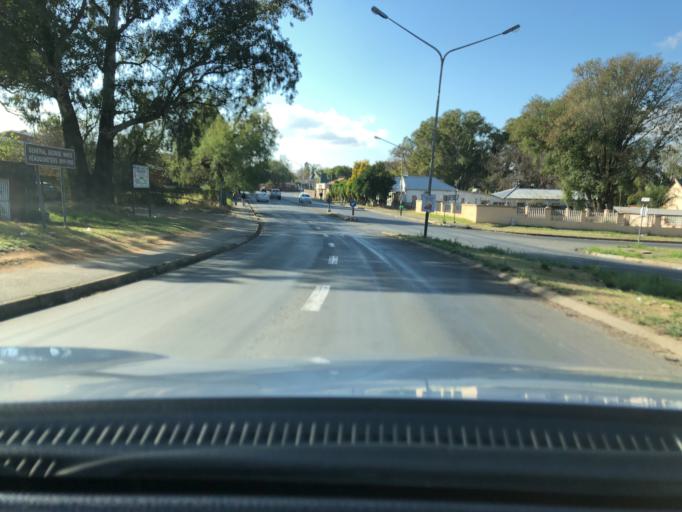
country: ZA
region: KwaZulu-Natal
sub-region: uThukela District Municipality
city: Ladysmith
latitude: -28.5590
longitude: 29.7747
